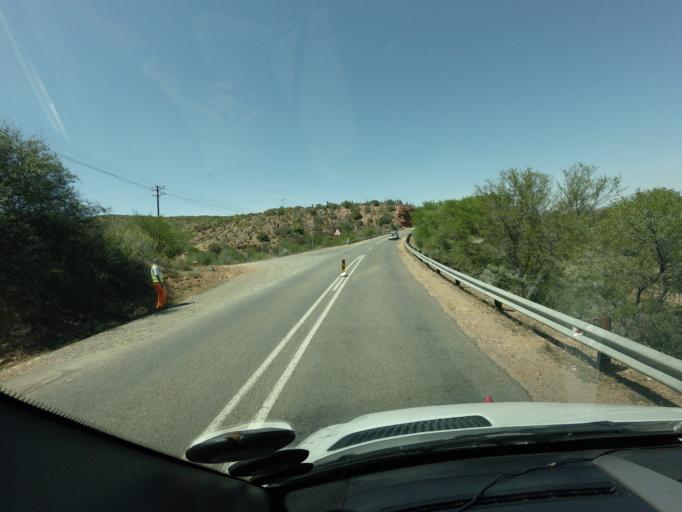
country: ZA
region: Western Cape
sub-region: Eden District Municipality
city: Oudtshoorn
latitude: -33.4891
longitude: 22.2476
